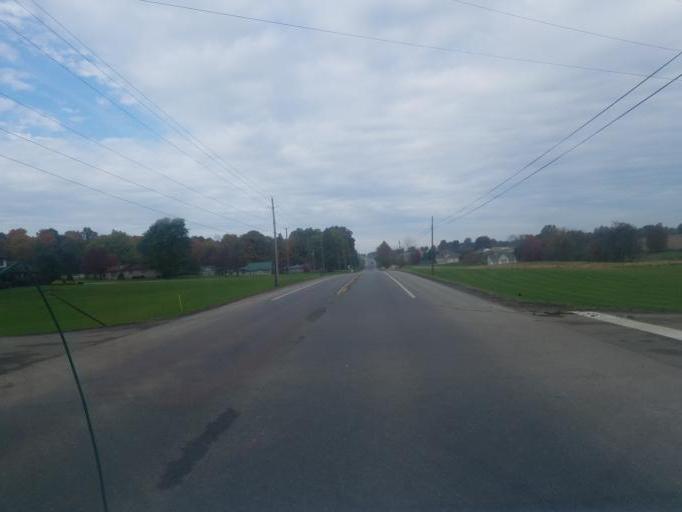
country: US
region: Ohio
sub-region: Wayne County
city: Dalton
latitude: 40.7053
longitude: -81.7310
